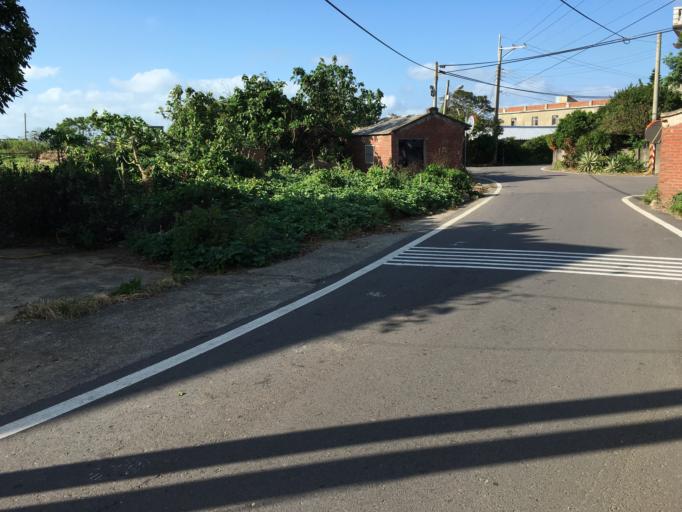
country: TW
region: Taiwan
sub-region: Hsinchu
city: Zhubei
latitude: 24.9249
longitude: 120.9841
